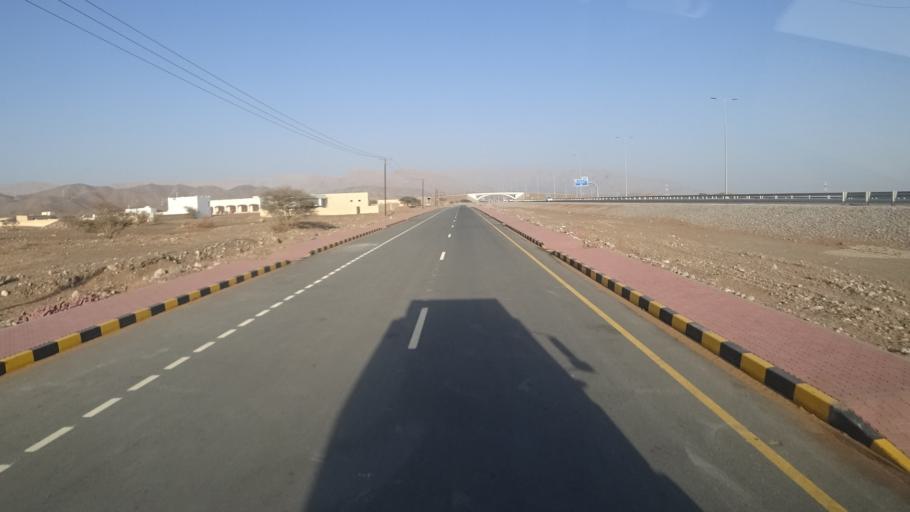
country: OM
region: Ash Sharqiyah
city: Badiyah
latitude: 22.4948
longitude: 58.9401
